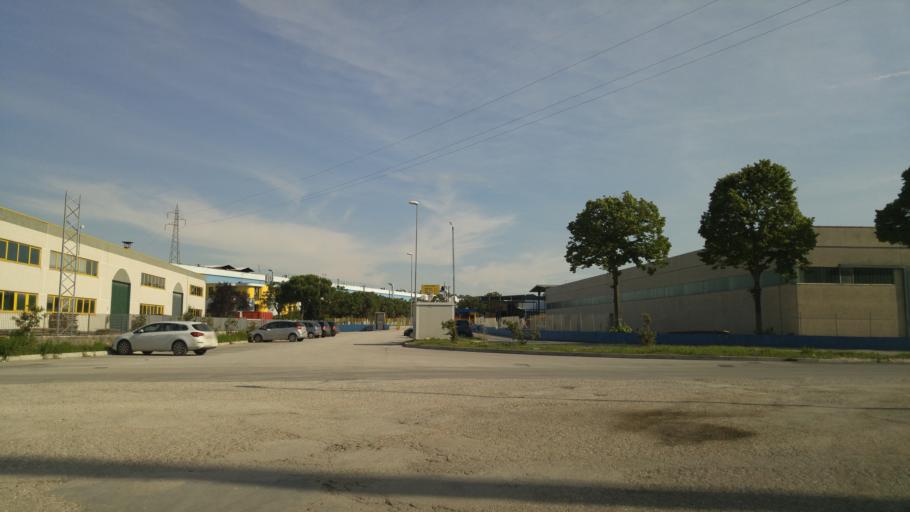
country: IT
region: The Marches
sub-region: Provincia di Pesaro e Urbino
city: Bellocchi
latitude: 43.7942
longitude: 13.0119
